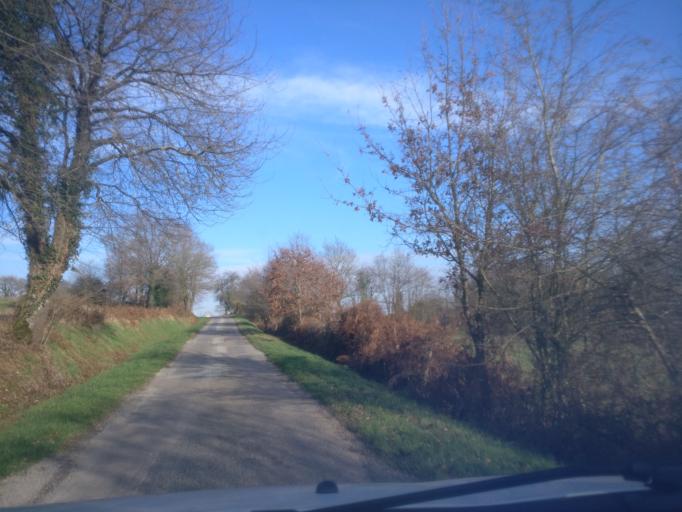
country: FR
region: Brittany
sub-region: Departement d'Ille-et-Vilaine
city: Livre-sur-Changeon
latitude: 48.2276
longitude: -1.3635
